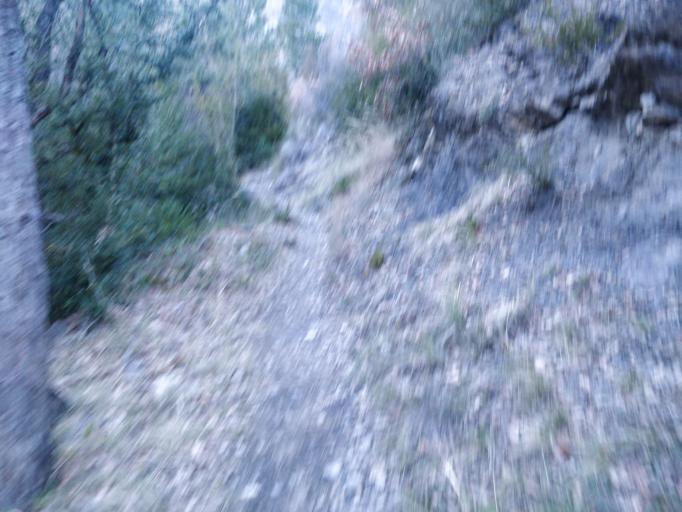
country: FR
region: Provence-Alpes-Cote d'Azur
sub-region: Departement des Alpes-de-Haute-Provence
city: Digne-les-Bains
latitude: 44.1027
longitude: 6.2481
